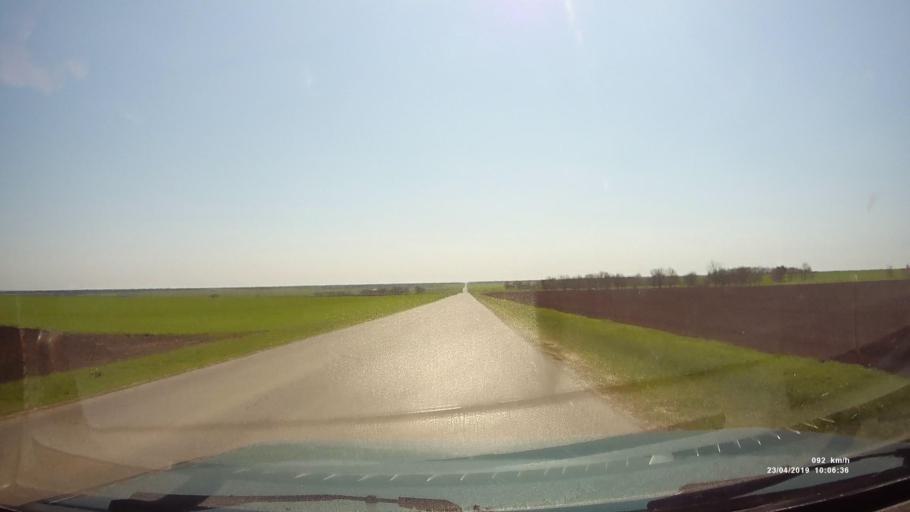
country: RU
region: Rostov
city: Sovetskoye
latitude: 46.7315
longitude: 42.2399
